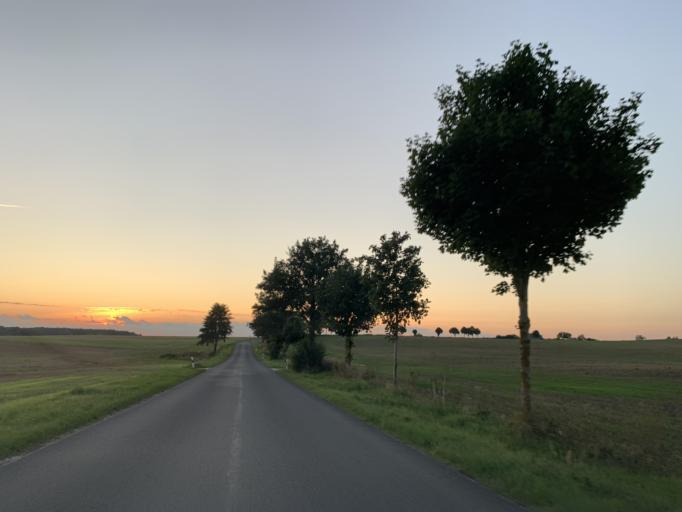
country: DE
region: Mecklenburg-Vorpommern
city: Blankensee
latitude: 53.4476
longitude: 13.2904
